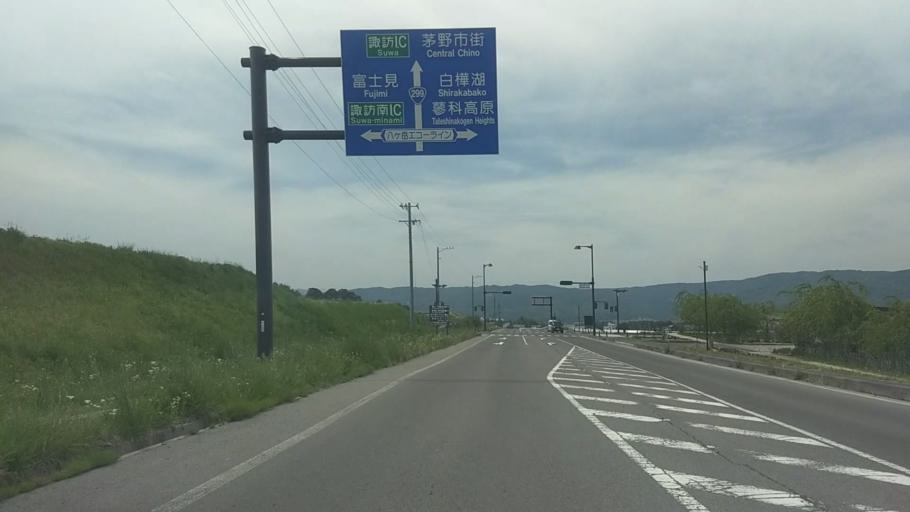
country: JP
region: Nagano
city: Chino
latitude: 36.0251
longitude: 138.2254
